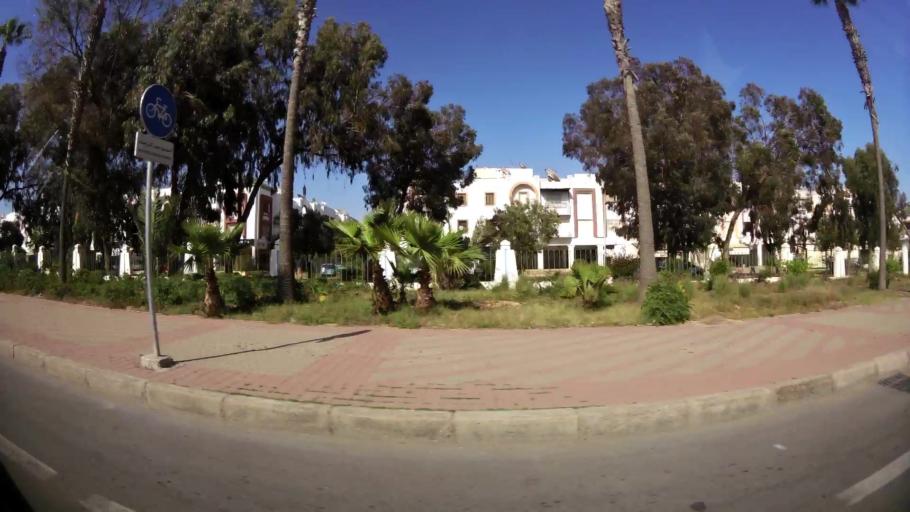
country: MA
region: Oued ed Dahab-Lagouira
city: Dakhla
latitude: 30.3883
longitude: -9.5744
